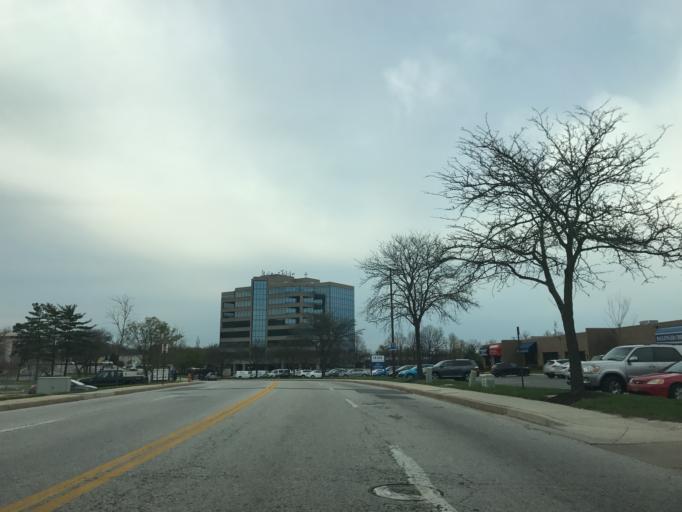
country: US
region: Maryland
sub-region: Baltimore County
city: Mays Chapel
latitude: 39.4523
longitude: -76.6385
